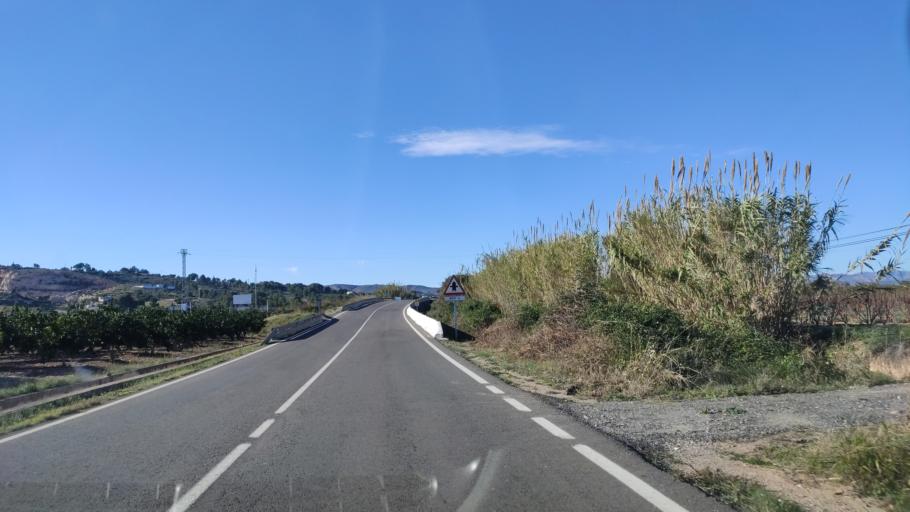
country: ES
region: Valencia
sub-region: Provincia de Valencia
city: Alberic
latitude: 39.1216
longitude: -0.5441
